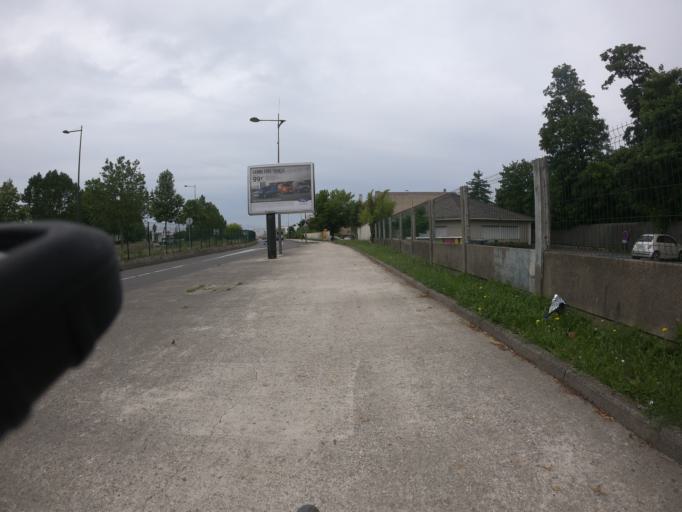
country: FR
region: Ile-de-France
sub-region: Departement du Val-de-Marne
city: Chevilly-Larue
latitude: 48.7695
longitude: 2.3516
